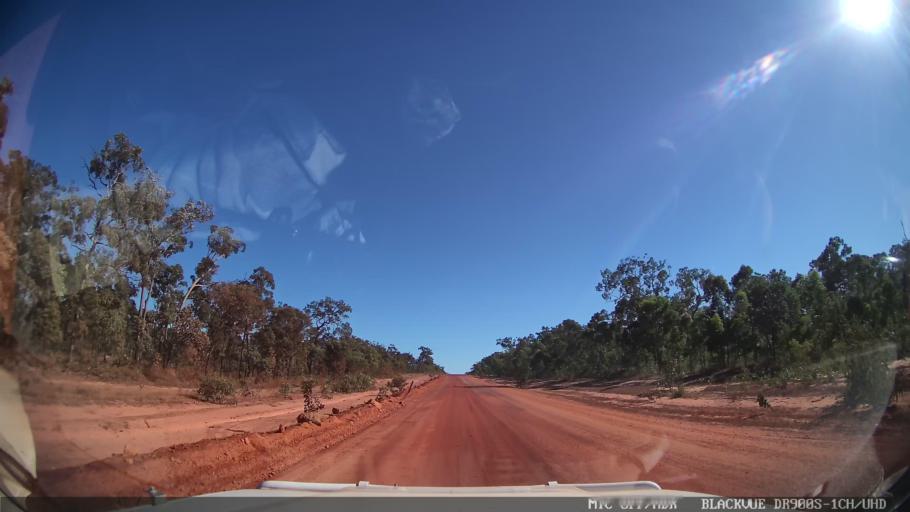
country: AU
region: Queensland
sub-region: Torres
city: Thursday Island
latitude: -11.3977
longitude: 142.3571
